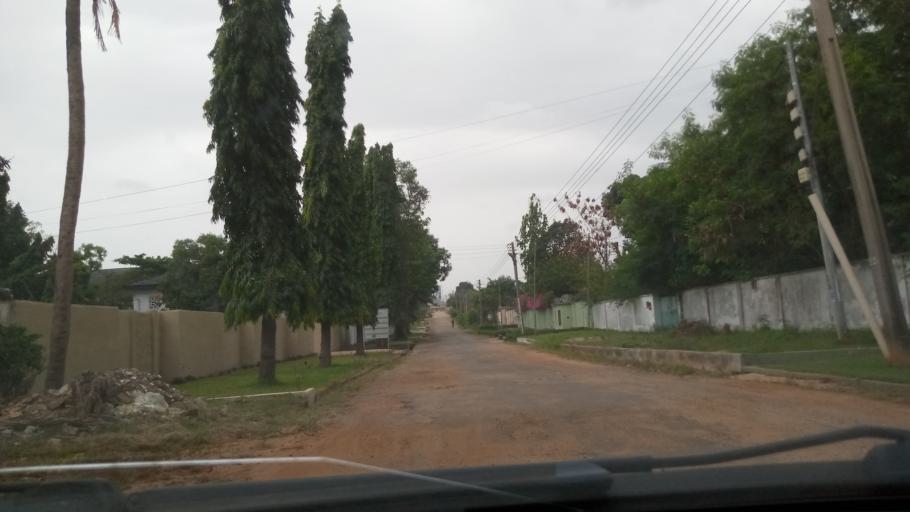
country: GH
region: Greater Accra
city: Dome
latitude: 5.6143
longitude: -0.2095
